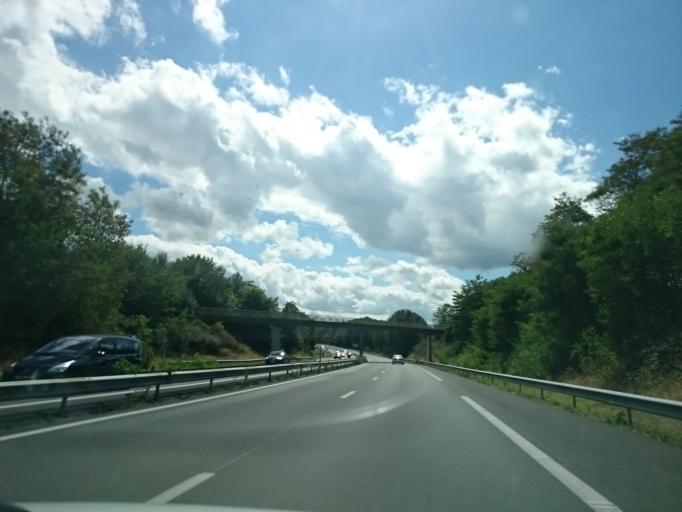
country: FR
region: Pays de la Loire
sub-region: Departement de Maine-et-Loire
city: Seiches-sur-le-Loir
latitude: 47.5814
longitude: -0.3332
